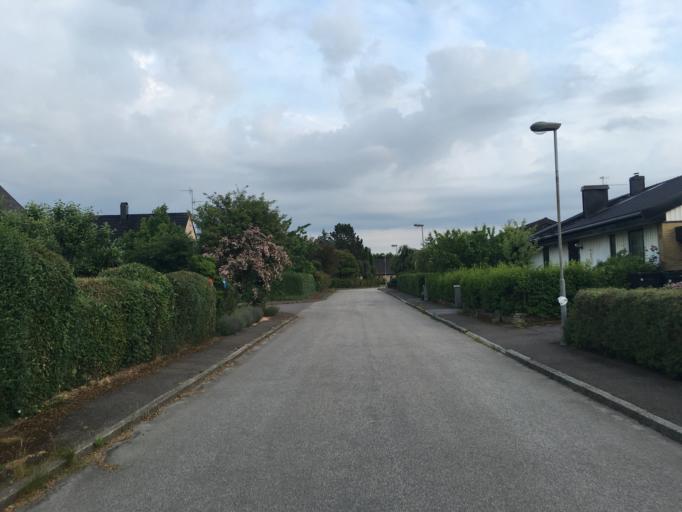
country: SE
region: Skane
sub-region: Lunds Kommun
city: Lund
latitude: 55.7472
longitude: 13.1934
